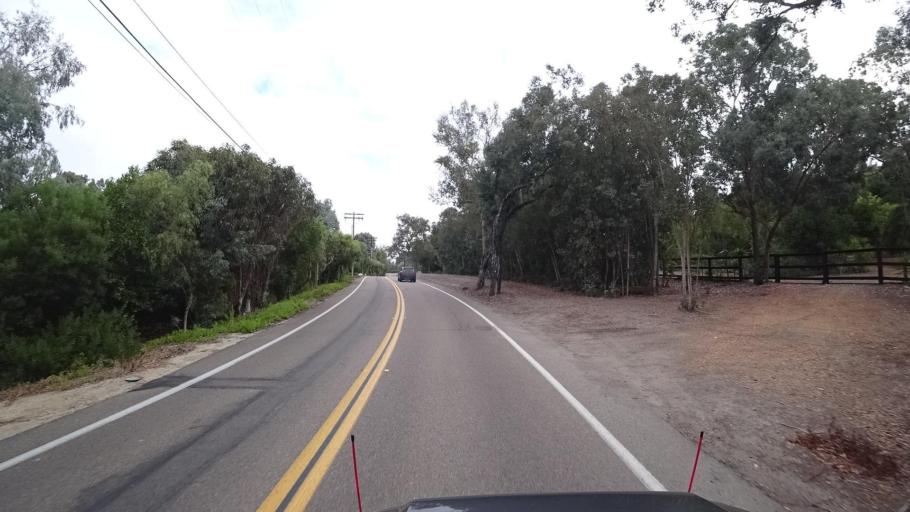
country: US
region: California
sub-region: San Diego County
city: Rancho Santa Fe
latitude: 33.0233
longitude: -117.2387
